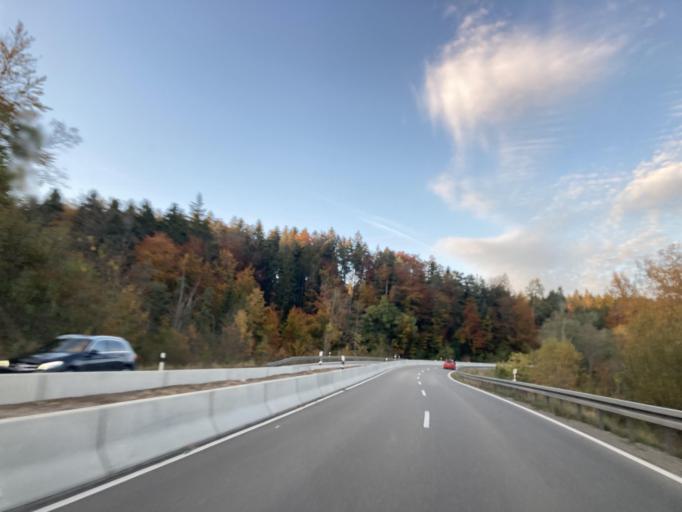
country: DE
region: Baden-Wuerttemberg
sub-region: Freiburg Region
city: Dietingen
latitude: 48.1902
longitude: 8.6850
